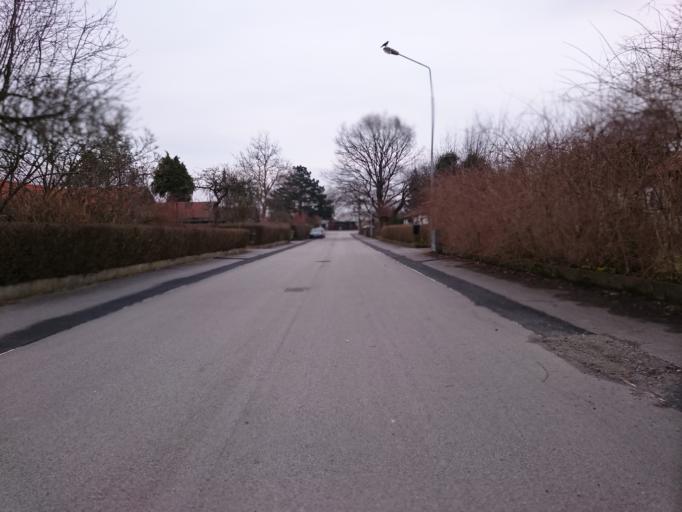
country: SE
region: Skane
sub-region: Staffanstorps Kommun
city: Hjaerup
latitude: 55.6665
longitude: 13.1497
